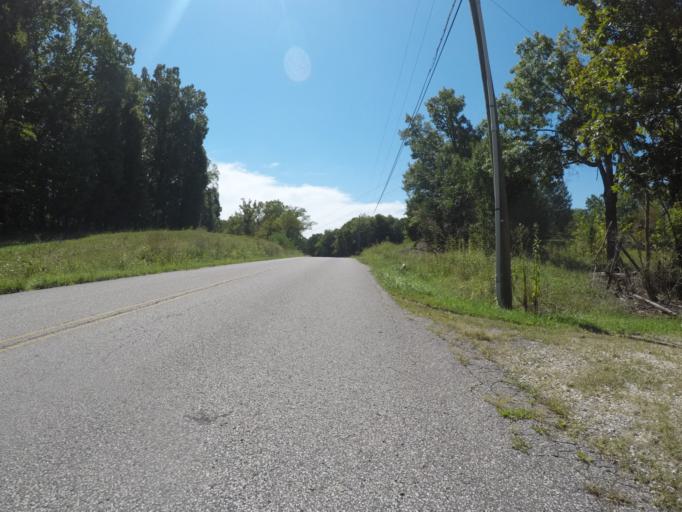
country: US
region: Kentucky
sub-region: Boyd County
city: Catlettsburg
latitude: 38.4094
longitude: -82.6542
